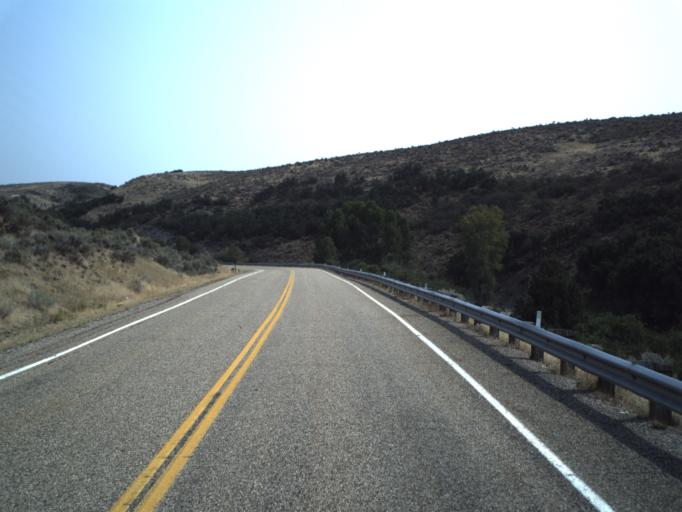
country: US
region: Utah
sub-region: Morgan County
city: Morgan
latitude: 40.9365
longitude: -111.5633
